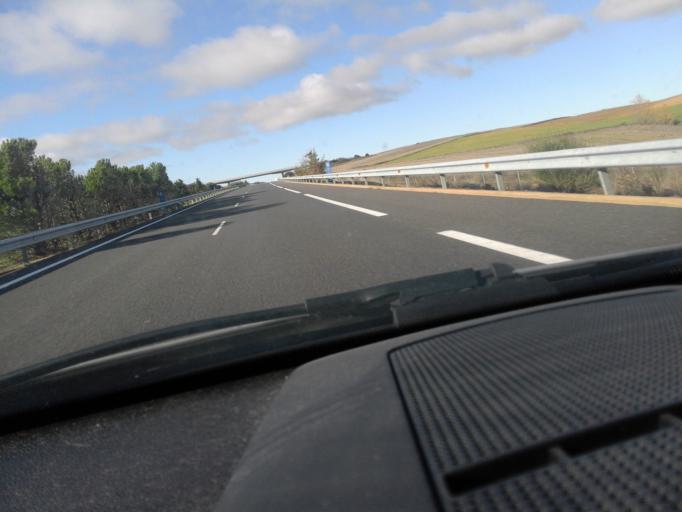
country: ES
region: Castille and Leon
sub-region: Provincia de Palencia
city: Moratinos
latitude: 42.3634
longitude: -4.9199
